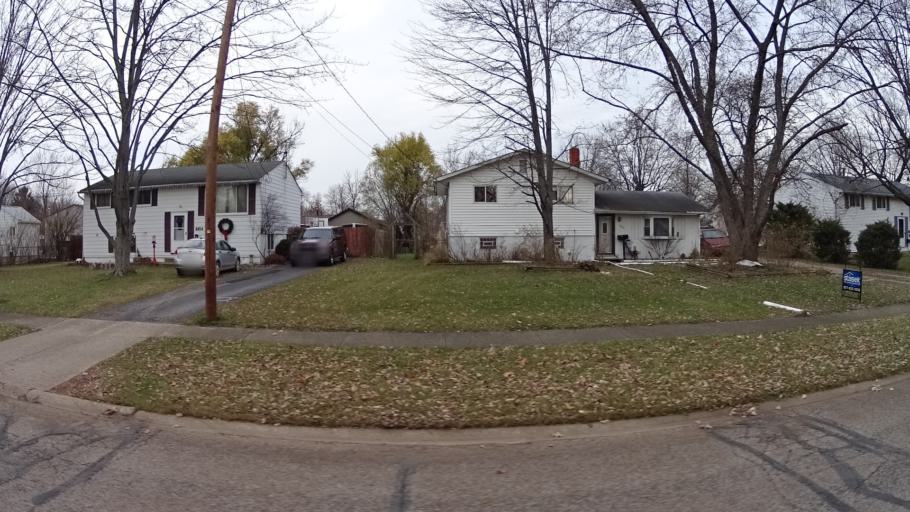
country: US
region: Ohio
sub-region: Lorain County
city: North Ridgeville
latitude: 41.3993
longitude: -82.0041
